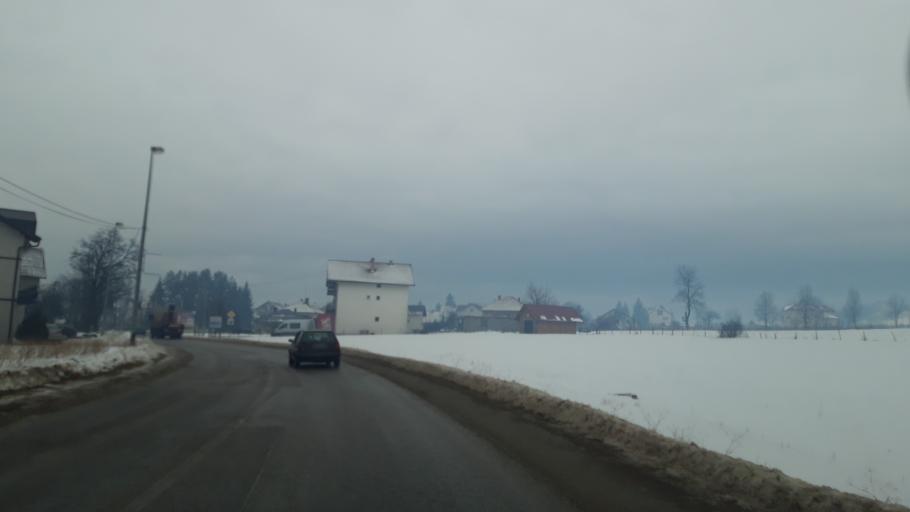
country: BA
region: Republika Srpska
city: Sokolac
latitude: 43.9335
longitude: 18.7900
